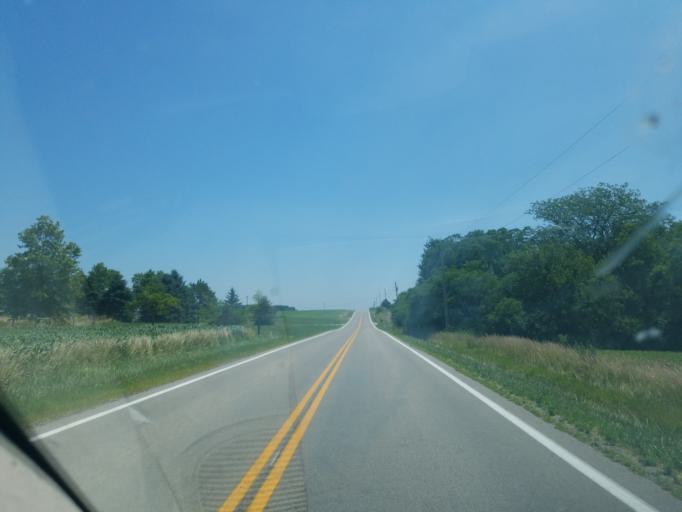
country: US
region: Ohio
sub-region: Mercer County
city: Rockford
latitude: 40.7424
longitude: -84.7040
